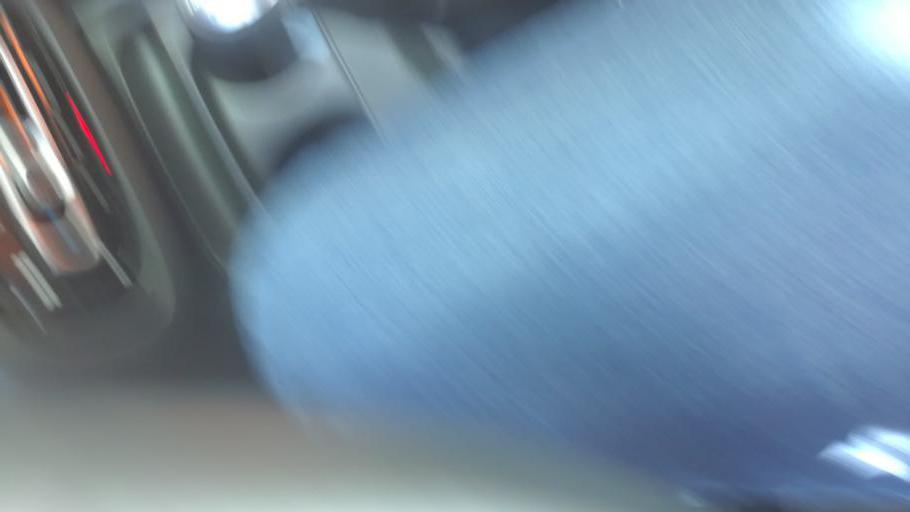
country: PT
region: Porto
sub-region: Maia
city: Nogueira
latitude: 41.2425
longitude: -8.5940
